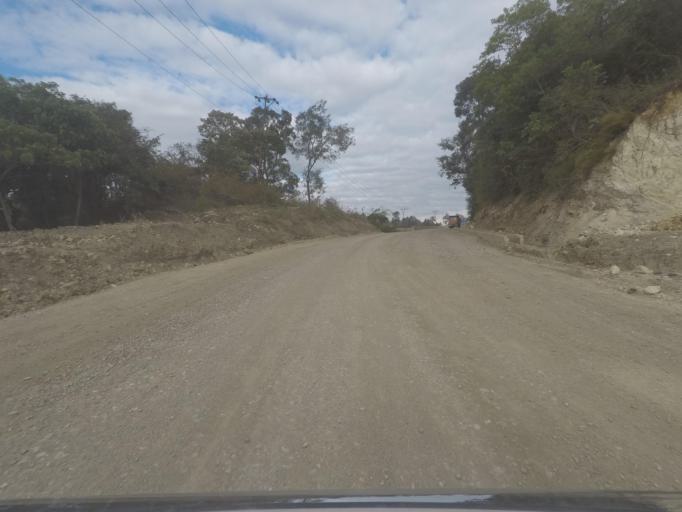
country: TL
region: Baucau
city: Venilale
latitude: -8.6340
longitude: 126.3798
